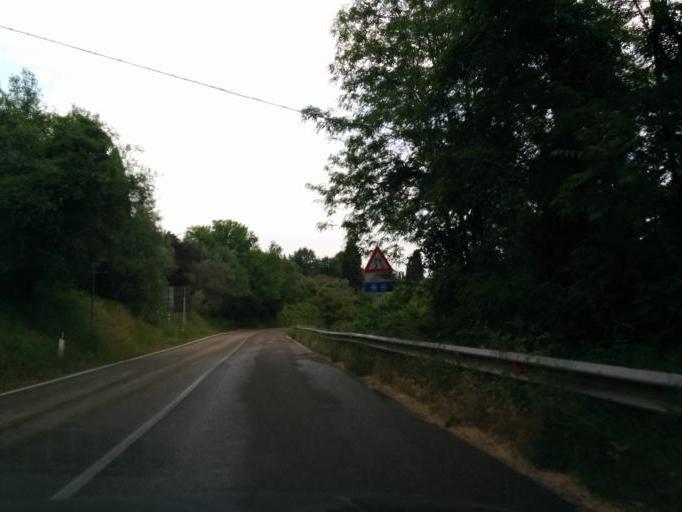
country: IT
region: Tuscany
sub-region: Province of Florence
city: San Casciano in Val di Pesa
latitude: 43.6632
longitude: 11.1916
